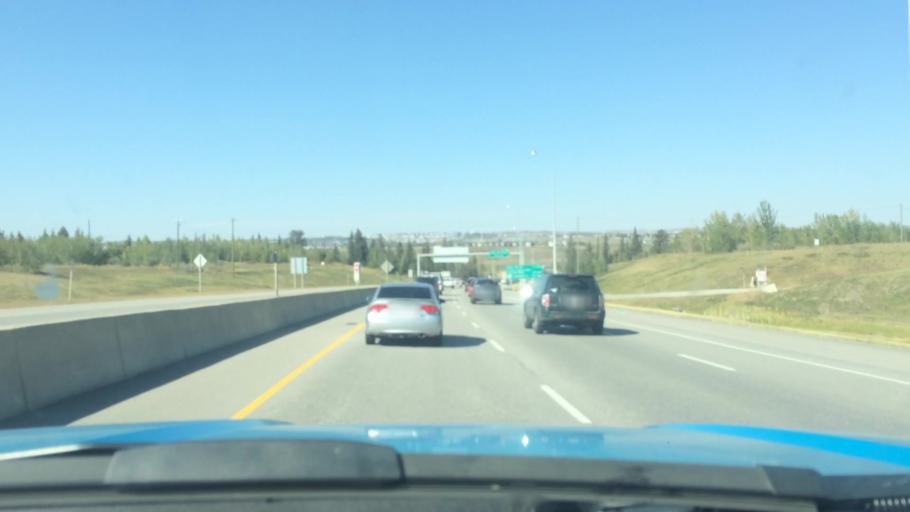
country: CA
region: Alberta
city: Calgary
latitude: 51.0929
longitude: -114.2333
